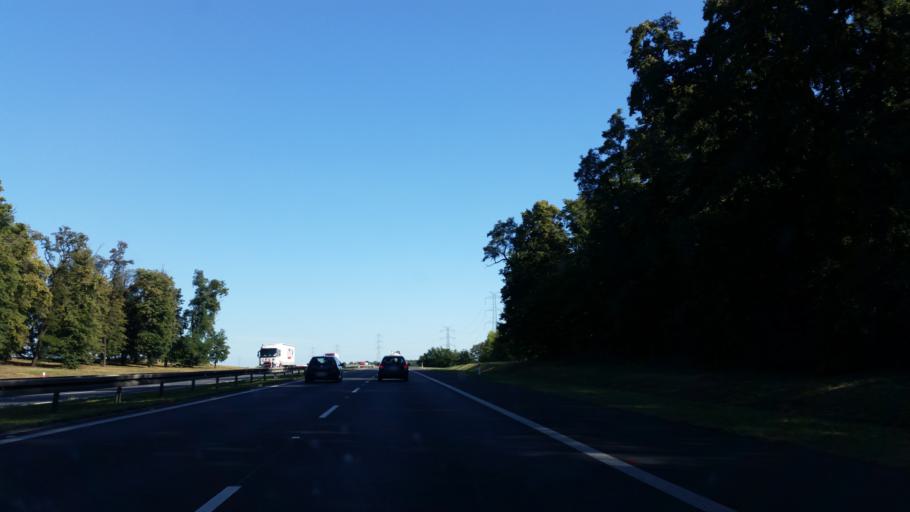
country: PL
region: Opole Voivodeship
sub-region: Powiat brzeski
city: Skarbimierz Osiedle
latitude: 50.8000
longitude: 17.3235
